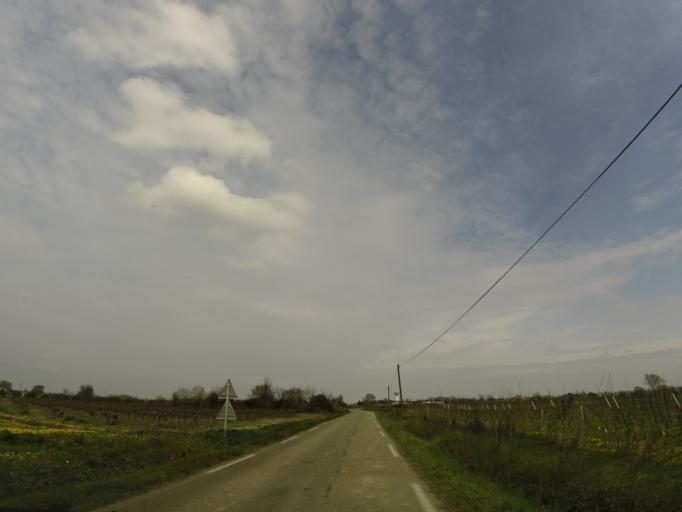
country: FR
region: Languedoc-Roussillon
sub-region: Departement du Gard
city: Aimargues
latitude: 43.6786
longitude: 4.1907
